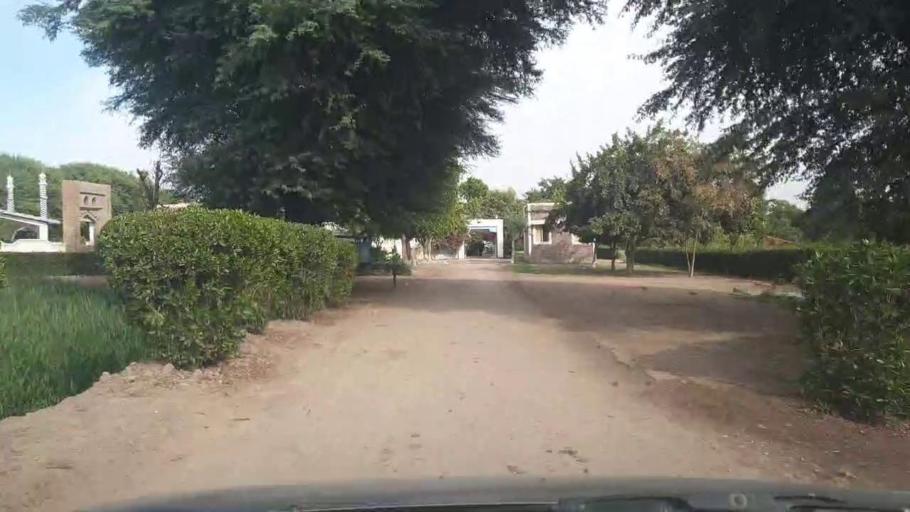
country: PK
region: Sindh
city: Kunri
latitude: 25.3065
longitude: 69.5755
